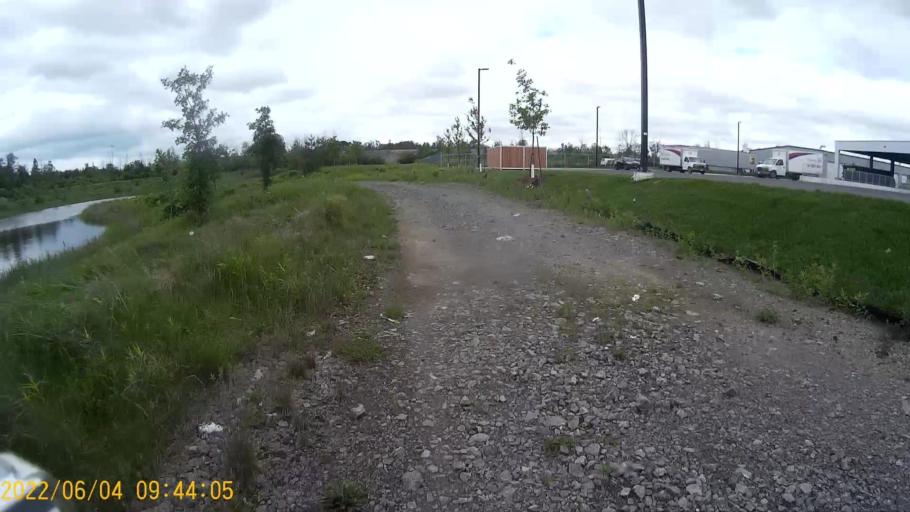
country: CA
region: Ontario
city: Bells Corners
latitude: 45.2924
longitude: -75.9444
